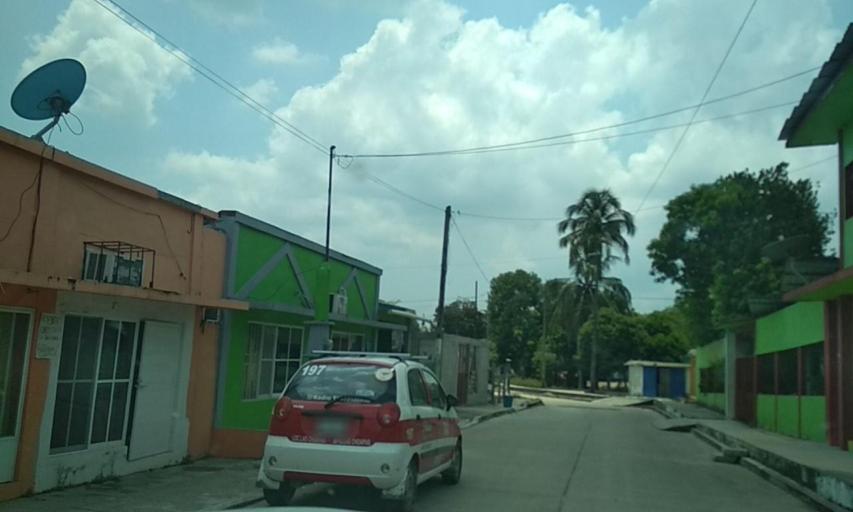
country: MX
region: Veracruz
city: Las Choapas
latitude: 17.9143
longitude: -94.0897
